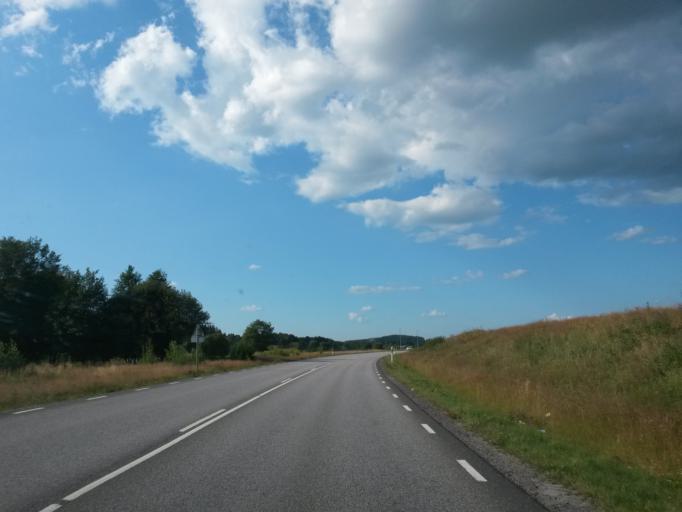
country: SE
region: Vaestra Goetaland
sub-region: Lerums Kommun
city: Stenkullen
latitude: 57.7848
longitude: 12.2962
